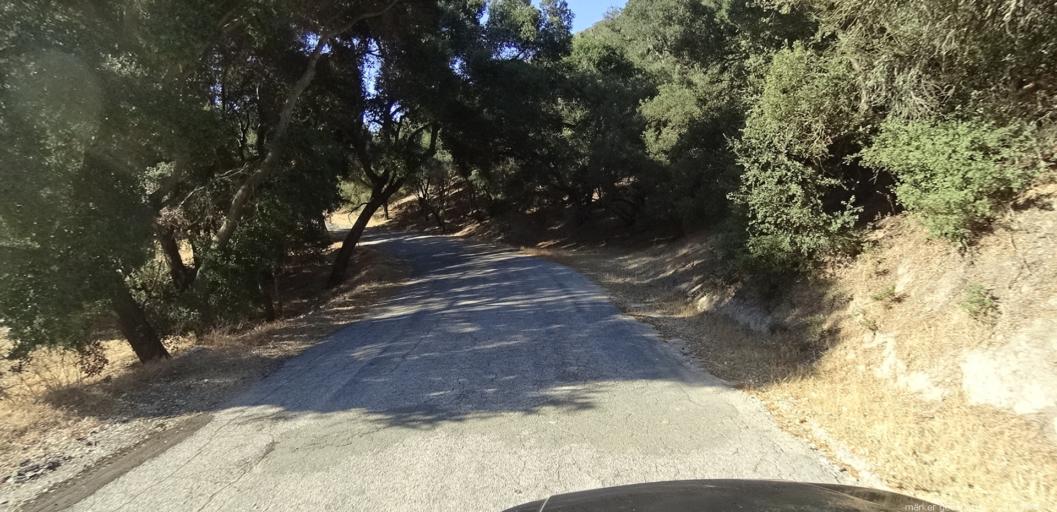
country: US
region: California
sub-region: Monterey County
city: Greenfield
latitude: 36.2009
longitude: -121.2764
